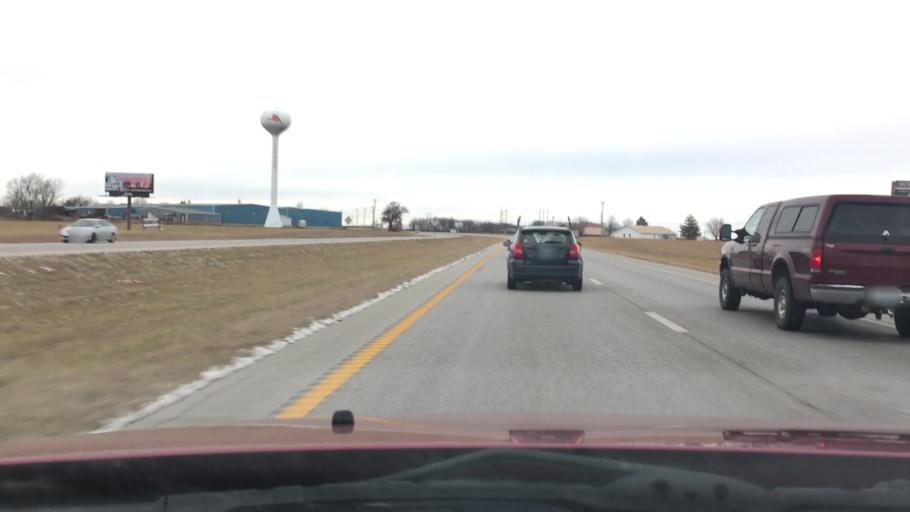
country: US
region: Missouri
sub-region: Webster County
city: Seymour
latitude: 37.1516
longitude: -92.7551
